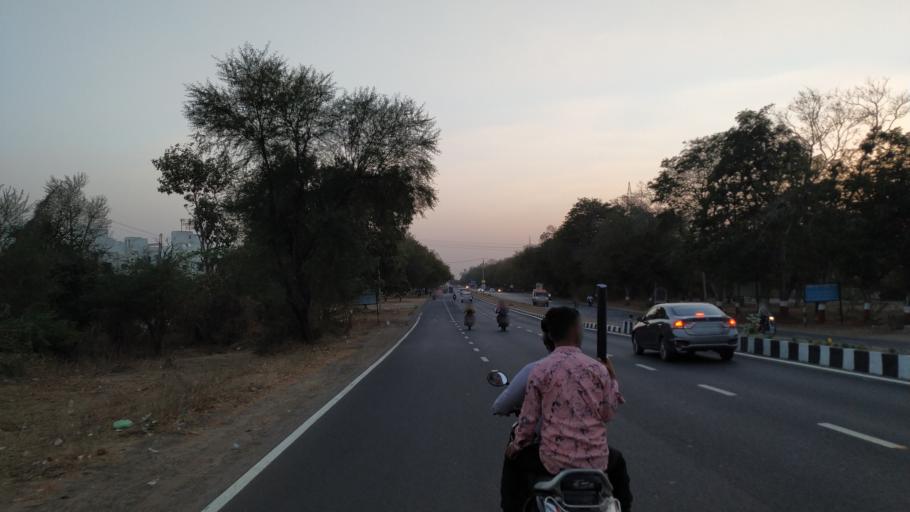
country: IN
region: Gujarat
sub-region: Gandhinagar
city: Adalaj
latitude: 23.1256
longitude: 72.6228
